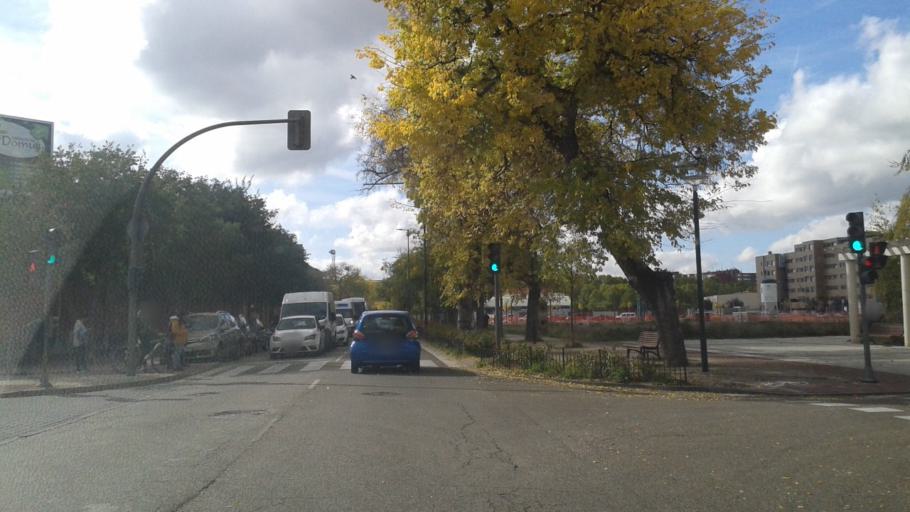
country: ES
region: Castille and Leon
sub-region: Provincia de Valladolid
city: Valladolid
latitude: 41.6628
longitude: -4.7091
